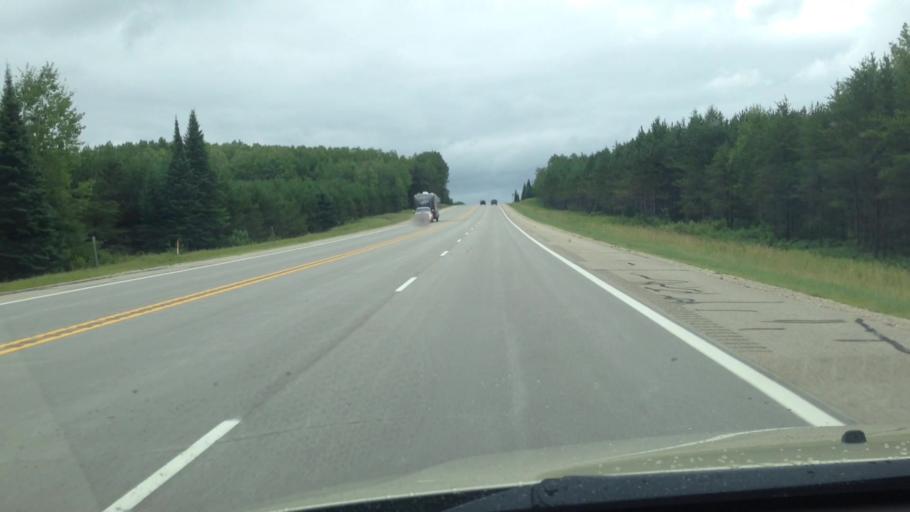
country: US
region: Michigan
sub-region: Schoolcraft County
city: Manistique
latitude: 45.9090
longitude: -86.4395
